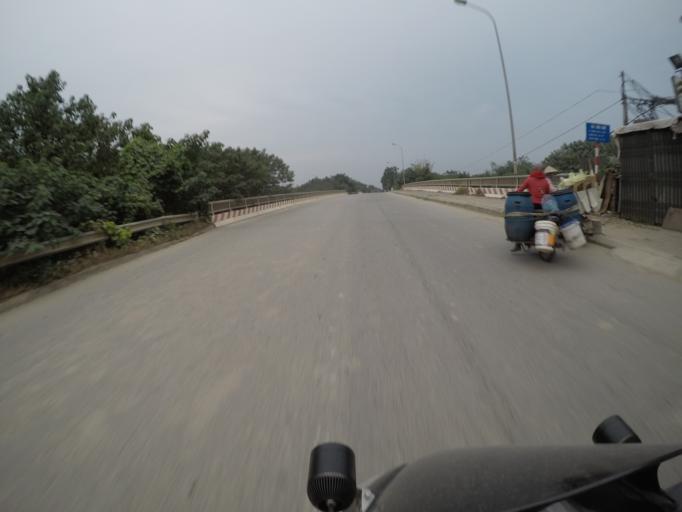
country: VN
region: Ha Noi
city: Cau Dien
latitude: 21.0068
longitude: 105.7633
